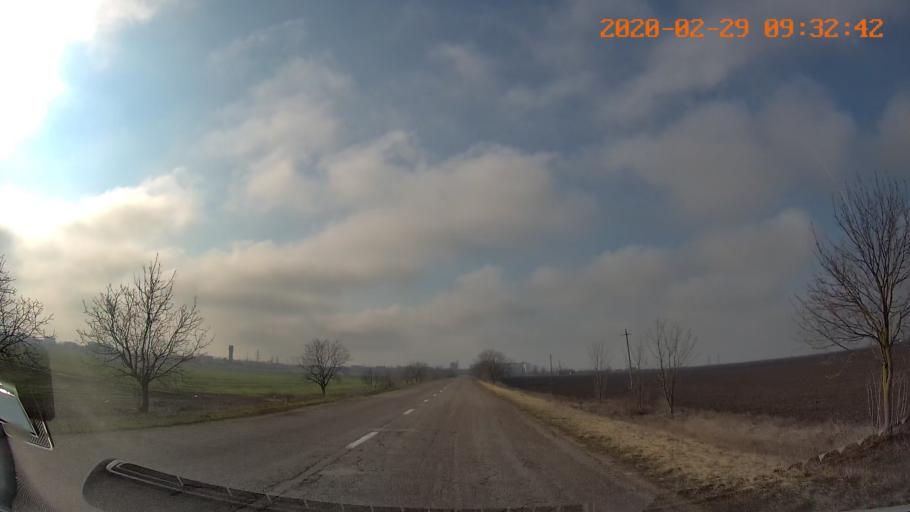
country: MD
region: Telenesti
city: Dnestrovsc
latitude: 46.6359
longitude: 29.9046
